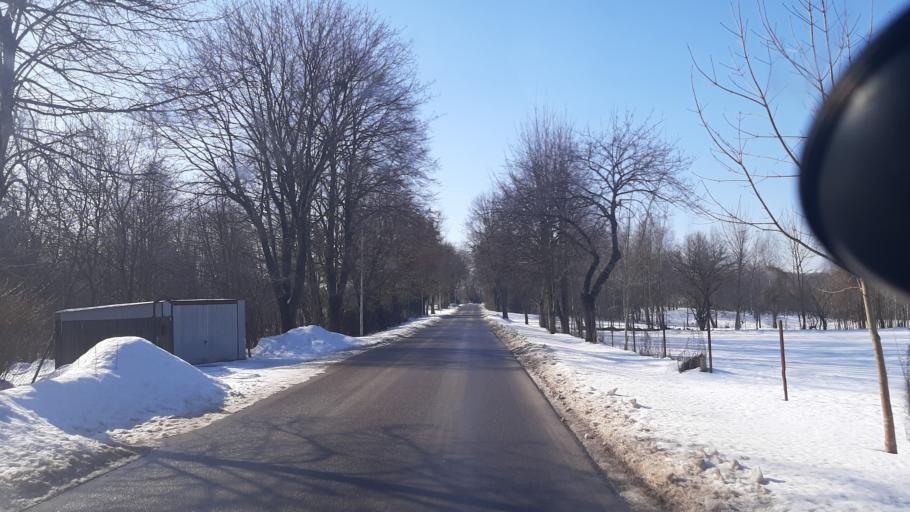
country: PL
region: Lublin Voivodeship
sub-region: Powiat pulawski
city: Naleczow
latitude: 51.2947
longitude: 22.2303
